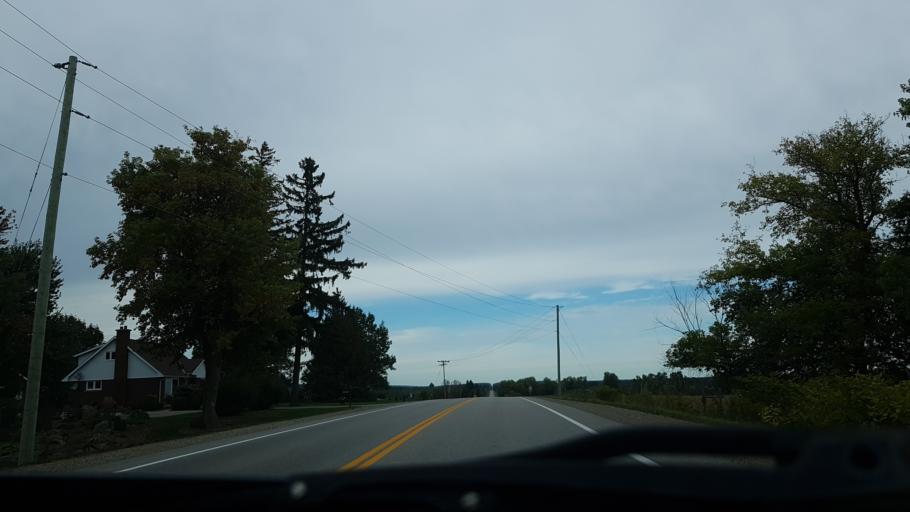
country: CA
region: Ontario
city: Shelburne
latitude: 44.1434
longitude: -80.0319
